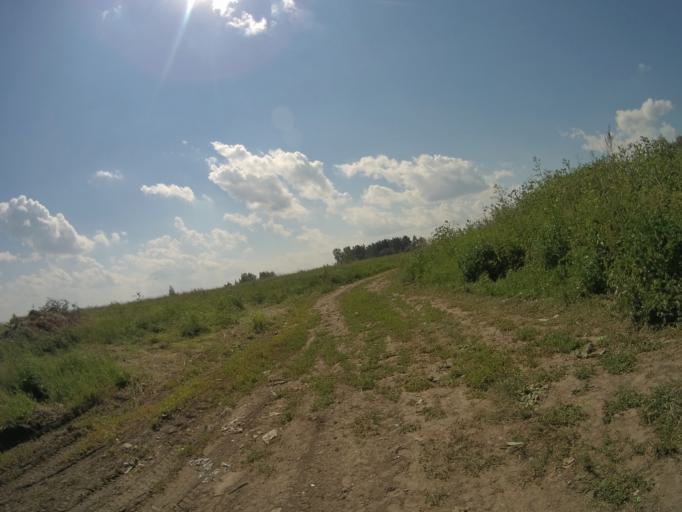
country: RU
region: Vladimir
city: Stavrovo
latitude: 56.1768
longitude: 40.1490
